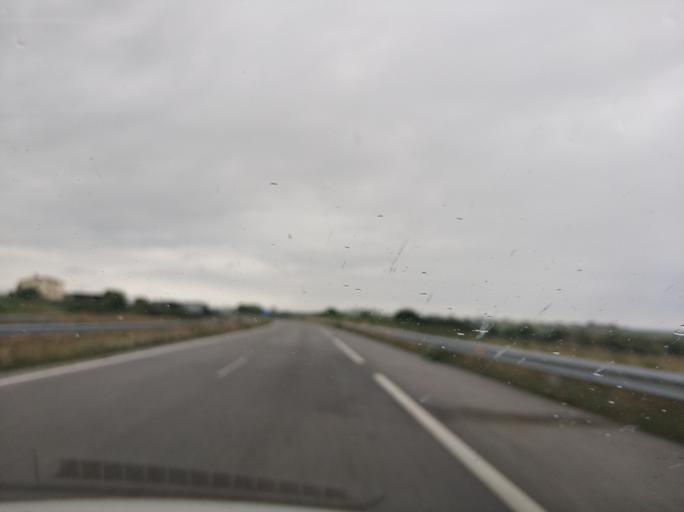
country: ES
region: Asturias
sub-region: Province of Asturias
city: Figueras
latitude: 43.5422
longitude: -6.9981
